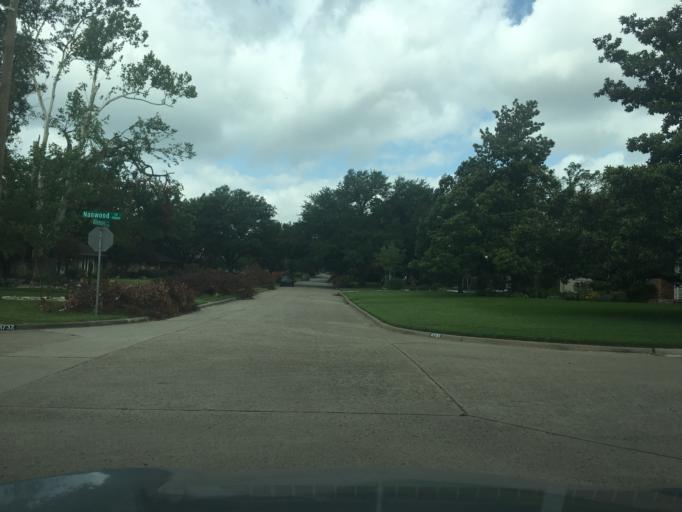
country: US
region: Texas
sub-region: Dallas County
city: Addison
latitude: 32.9109
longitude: -96.8260
